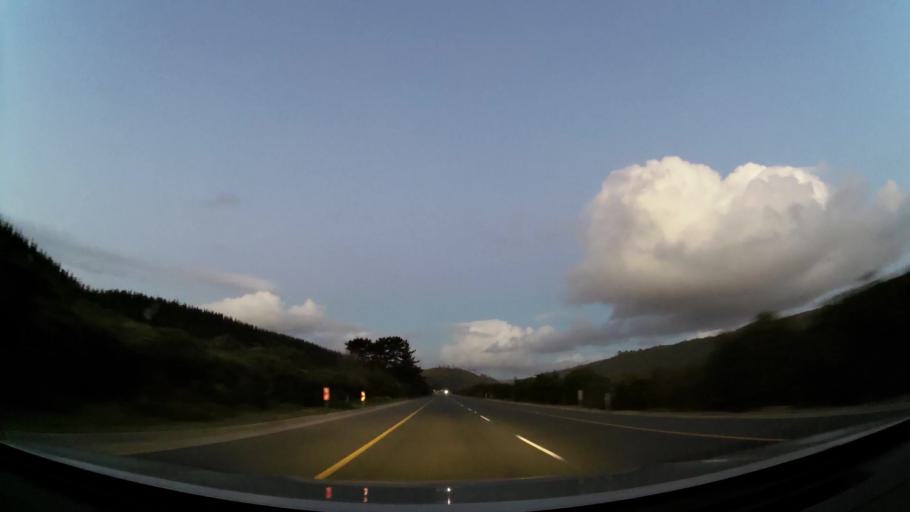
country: ZA
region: Western Cape
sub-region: Eden District Municipality
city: Knysna
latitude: -34.0250
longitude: 22.8683
